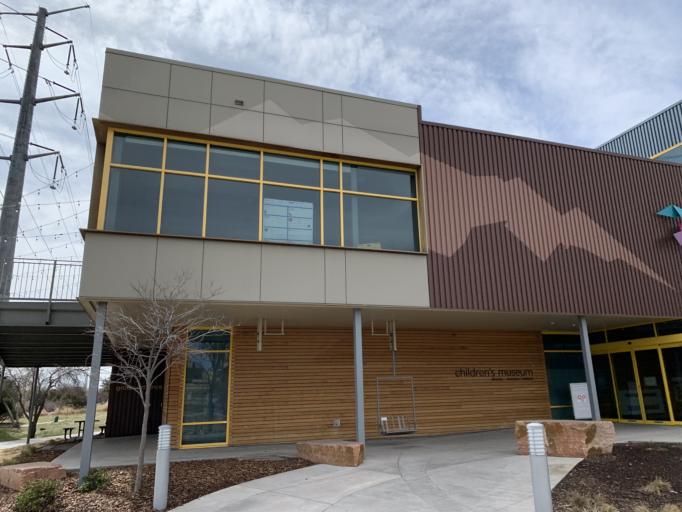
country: US
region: Colorado
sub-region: Denver County
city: Denver
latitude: 39.7488
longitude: -105.0166
